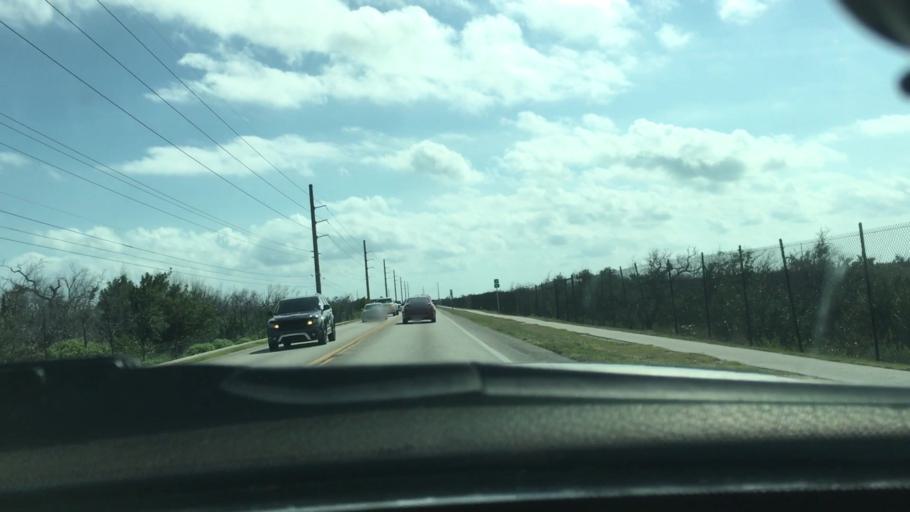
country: US
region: Florida
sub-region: Monroe County
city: Big Pine Key
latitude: 24.6589
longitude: -81.3376
